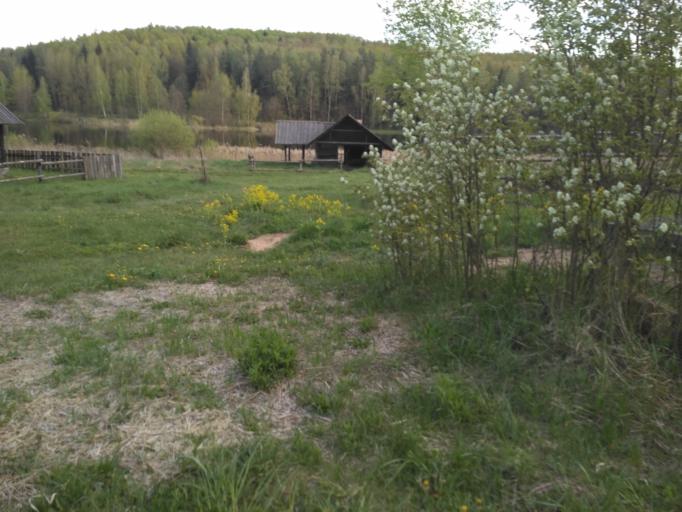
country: BY
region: Minsk
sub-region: Smalyavitski Rayon
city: Usjazh
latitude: 54.1030
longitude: 28.0526
